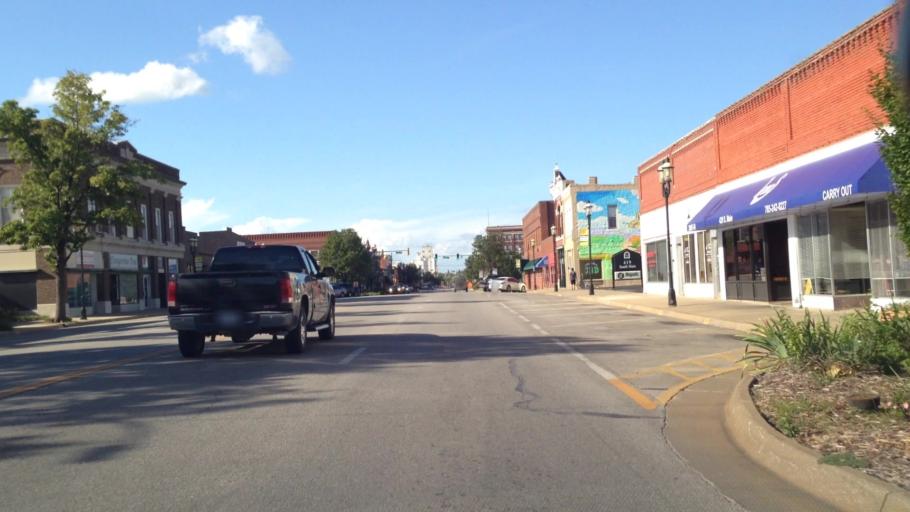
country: US
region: Kansas
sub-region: Franklin County
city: Ottawa
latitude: 38.6114
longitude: -95.2685
